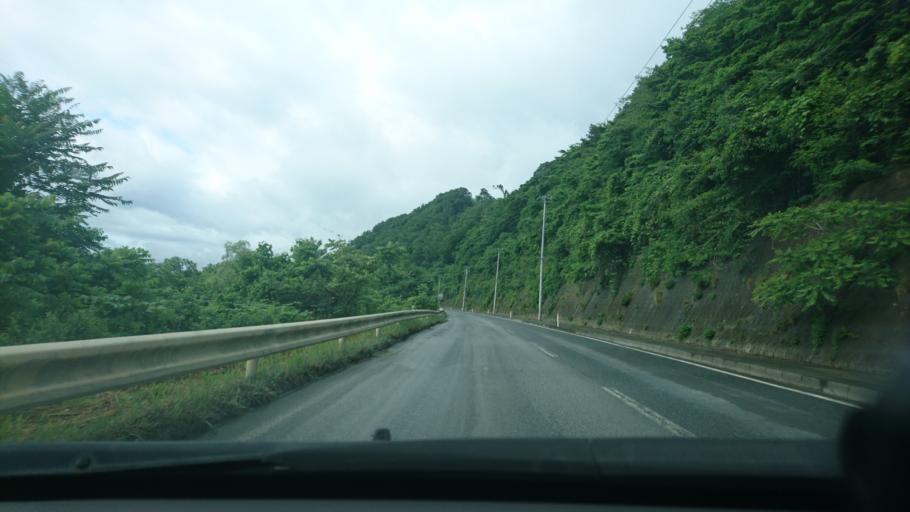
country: JP
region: Miyagi
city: Ishinomaki
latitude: 38.5820
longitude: 141.3035
